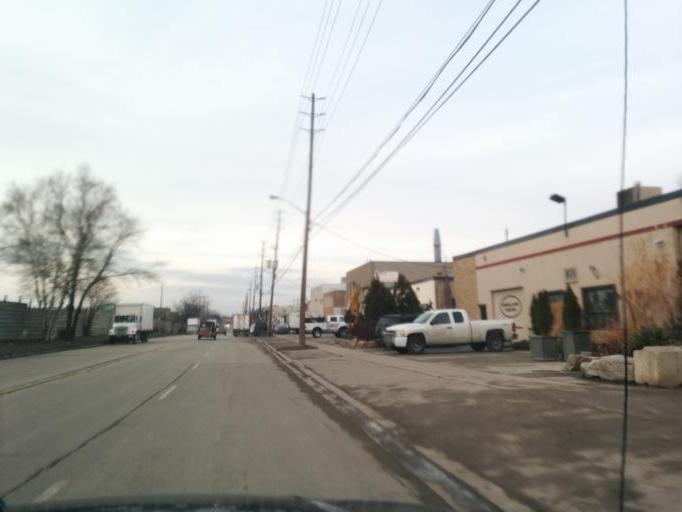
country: CA
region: Ontario
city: Etobicoke
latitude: 43.6231
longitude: -79.5408
